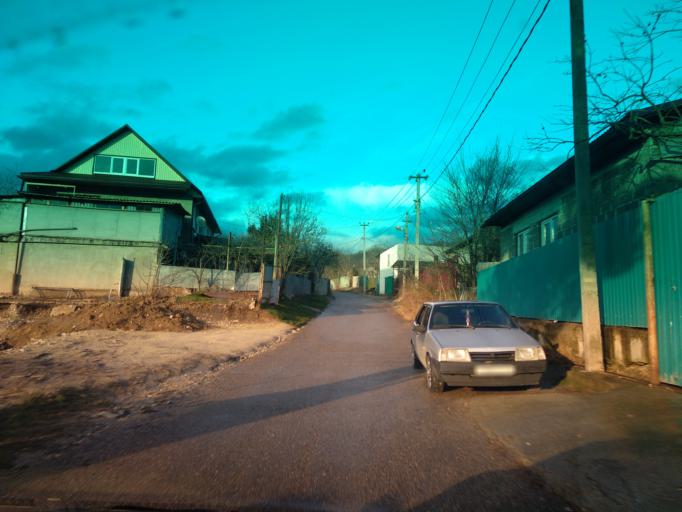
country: RU
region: Krasnodarskiy
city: Novomikhaylovskiy
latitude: 44.2736
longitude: 38.8337
